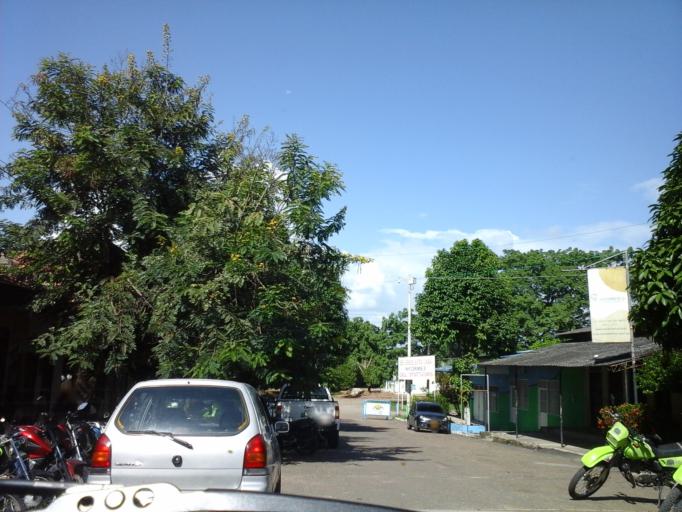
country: CO
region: Meta
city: Puerto Lopez
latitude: 4.0855
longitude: -72.9527
